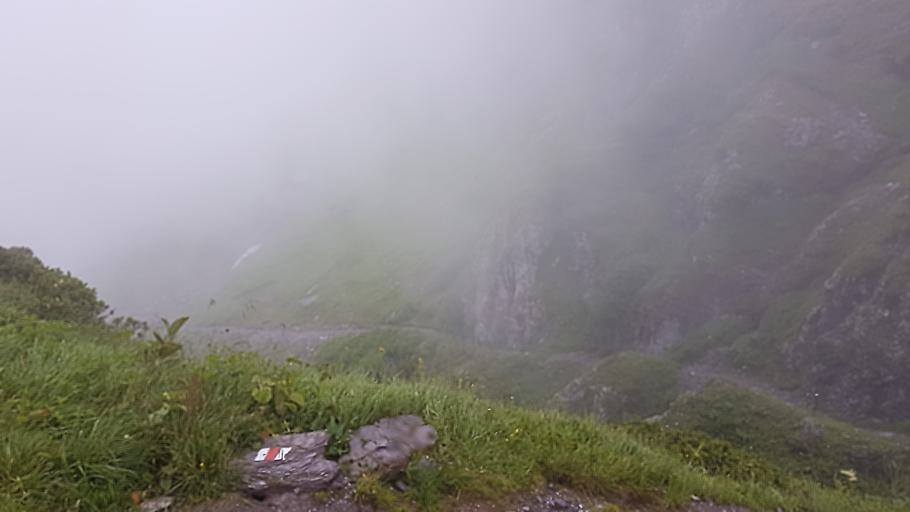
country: CH
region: Saint Gallen
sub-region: Wahlkreis Sarganserland
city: Sargans
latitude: 46.9899
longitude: 9.4083
